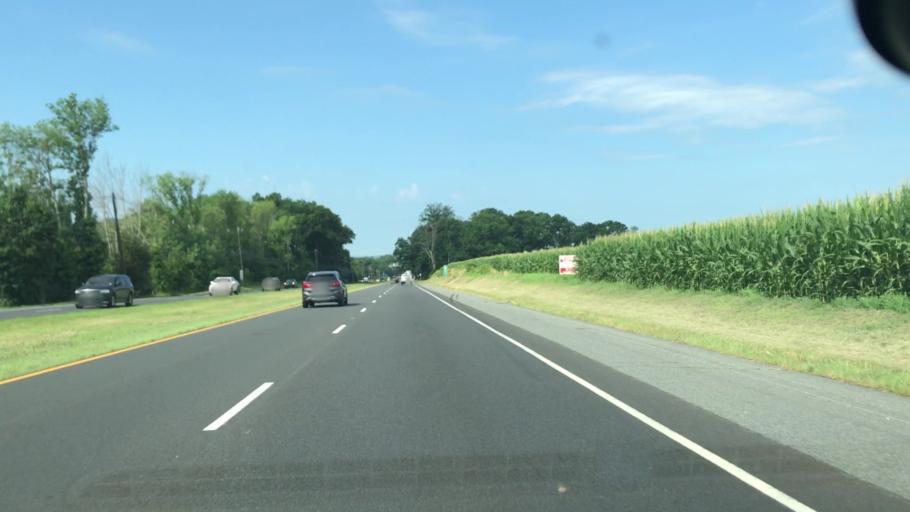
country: US
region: New Jersey
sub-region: Hunterdon County
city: Flemington
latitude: 40.5307
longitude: -74.7837
